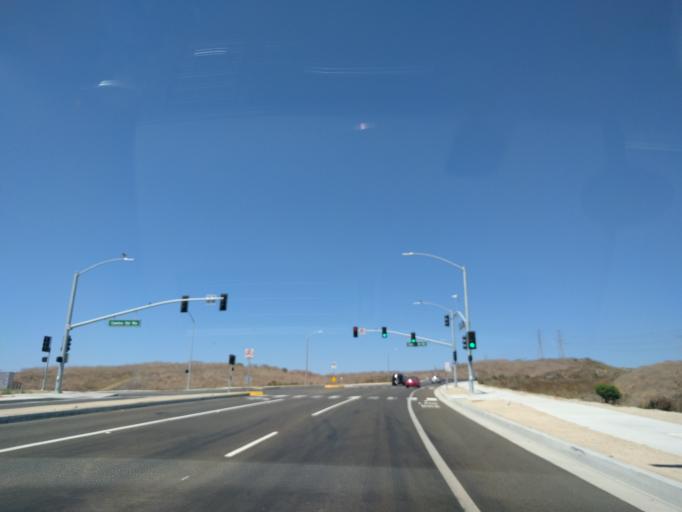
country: US
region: California
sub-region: Orange County
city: San Clemente
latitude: 33.4713
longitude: -117.6097
